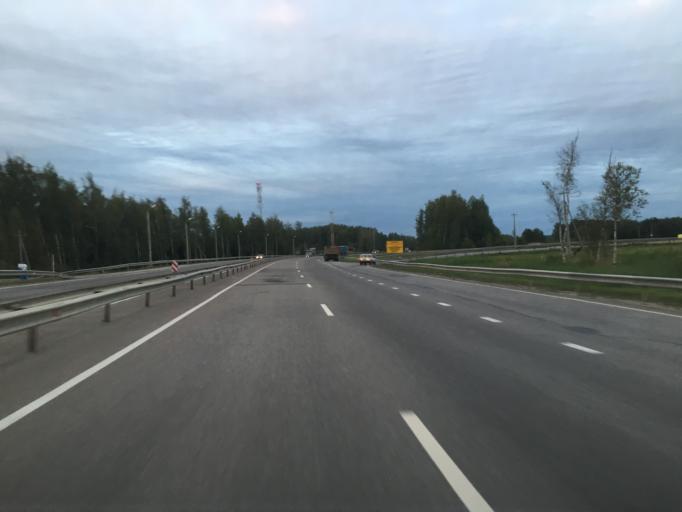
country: RU
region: Kaluga
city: Kaluga
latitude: 54.6271
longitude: 36.2888
